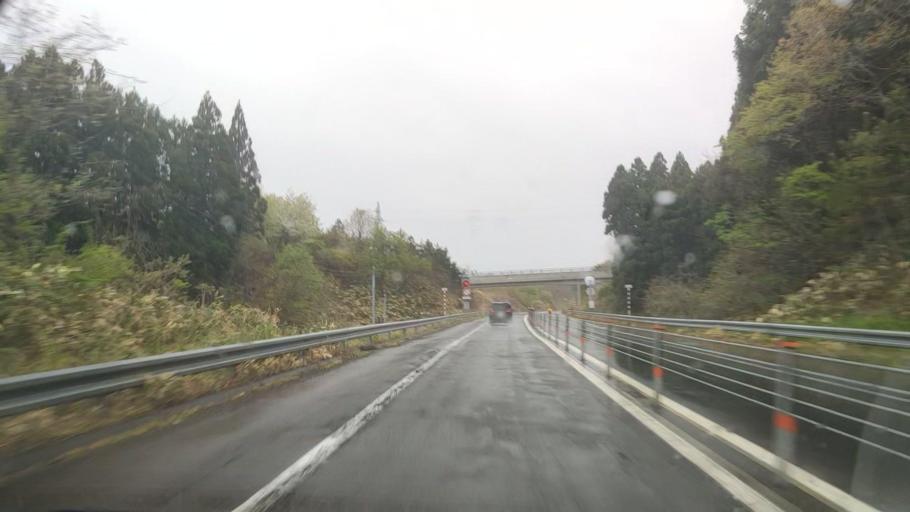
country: JP
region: Akita
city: Noshiromachi
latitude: 40.1659
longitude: 140.0485
